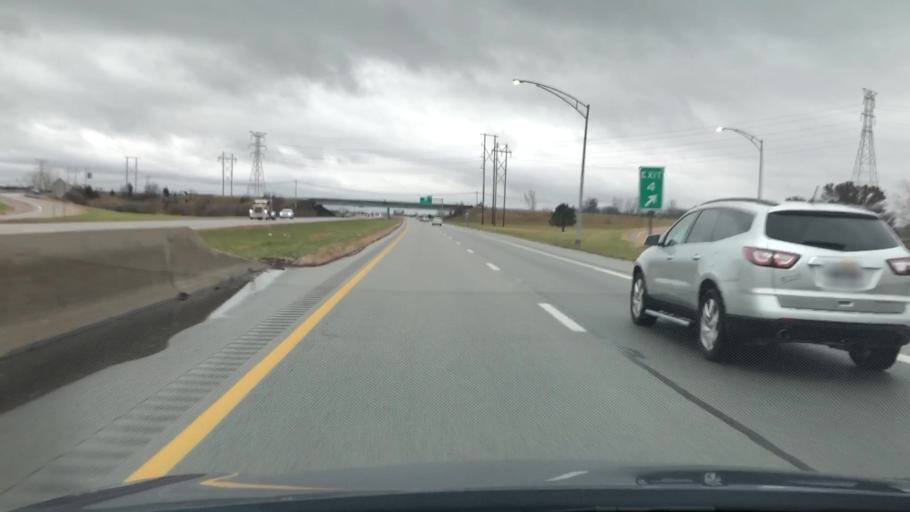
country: US
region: Ohio
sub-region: Wood County
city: Walbridge
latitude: 41.5909
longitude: -83.4770
